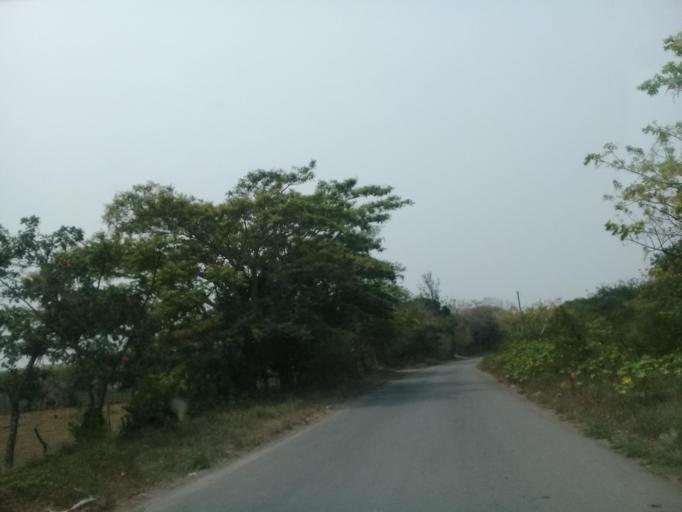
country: MX
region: Veracruz
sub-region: Medellin
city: La Laguna y Monte del Castillo
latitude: 18.9479
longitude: -96.1265
